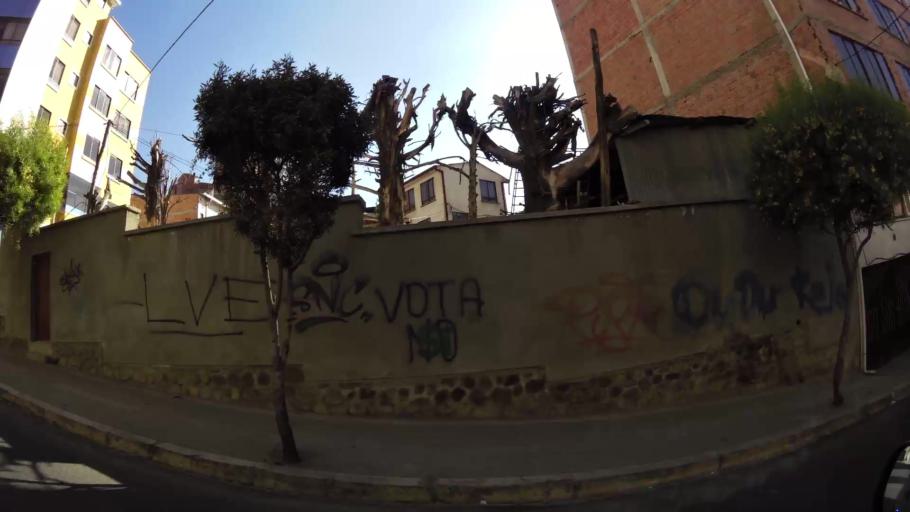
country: BO
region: La Paz
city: La Paz
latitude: -16.5074
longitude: -68.1356
